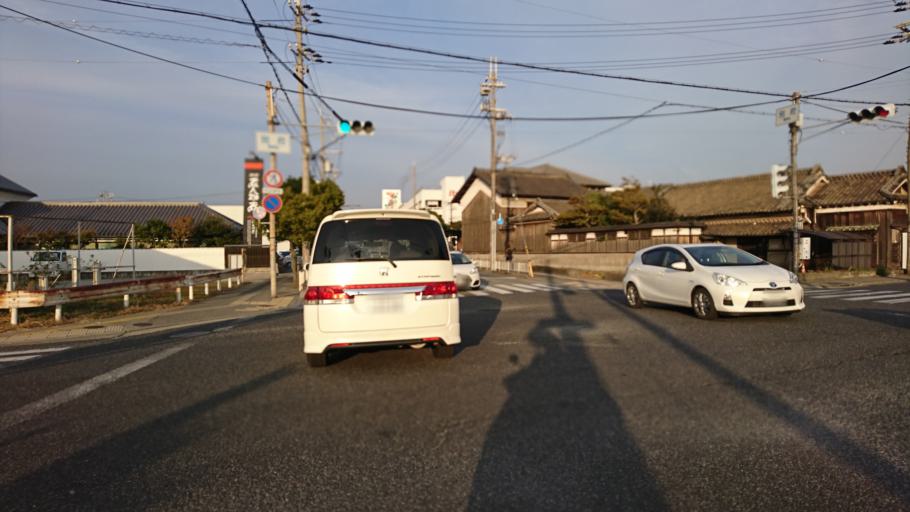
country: JP
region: Hyogo
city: Kakogawacho-honmachi
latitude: 34.7265
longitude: 134.8467
